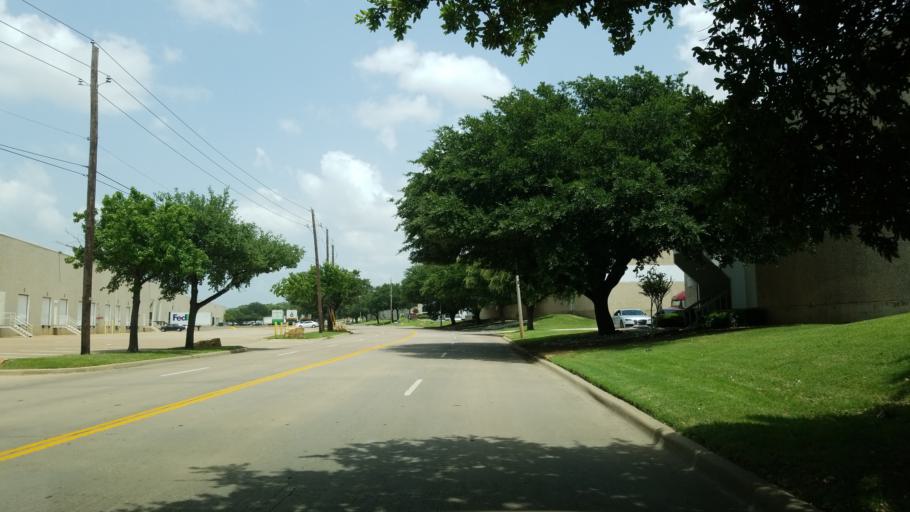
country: US
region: Texas
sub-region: Dallas County
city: Cockrell Hill
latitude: 32.7710
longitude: -96.8827
